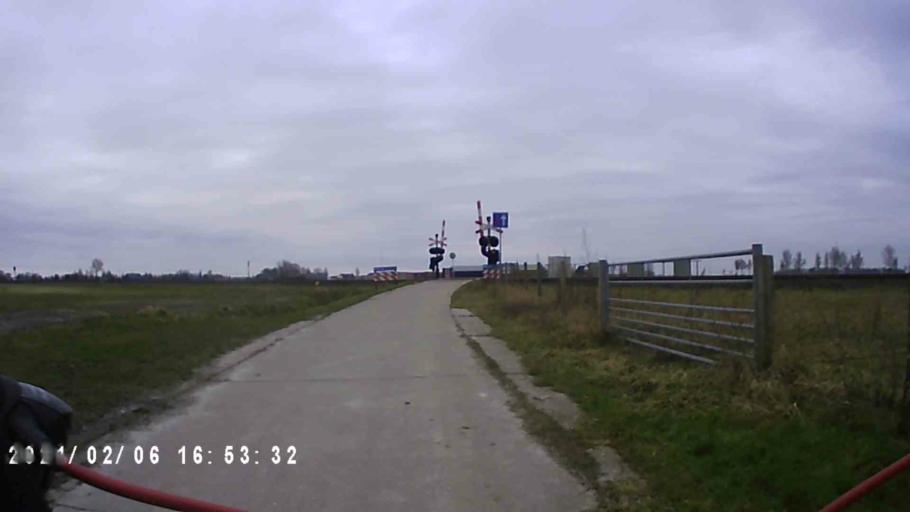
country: NL
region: Groningen
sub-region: Gemeente Appingedam
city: Appingedam
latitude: 53.4123
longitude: 6.7480
